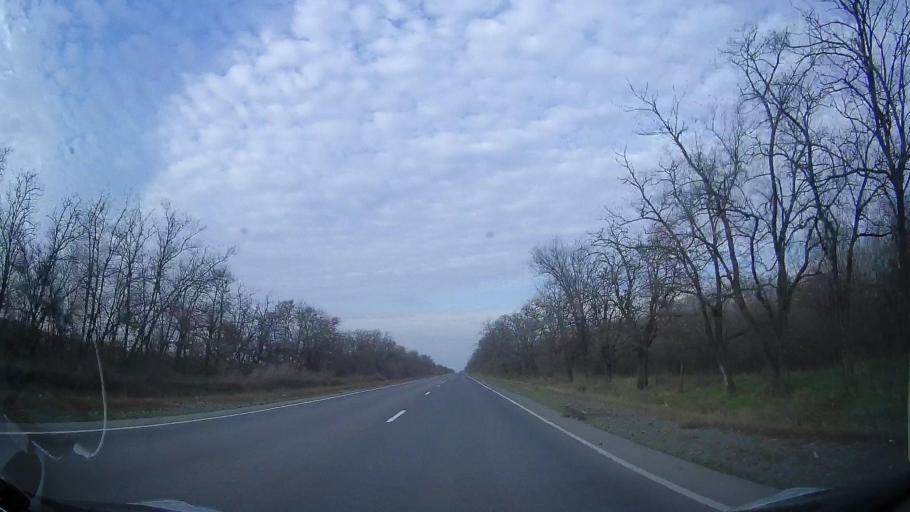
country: RU
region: Rostov
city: Bagayevskaya
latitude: 47.1230
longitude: 40.2767
